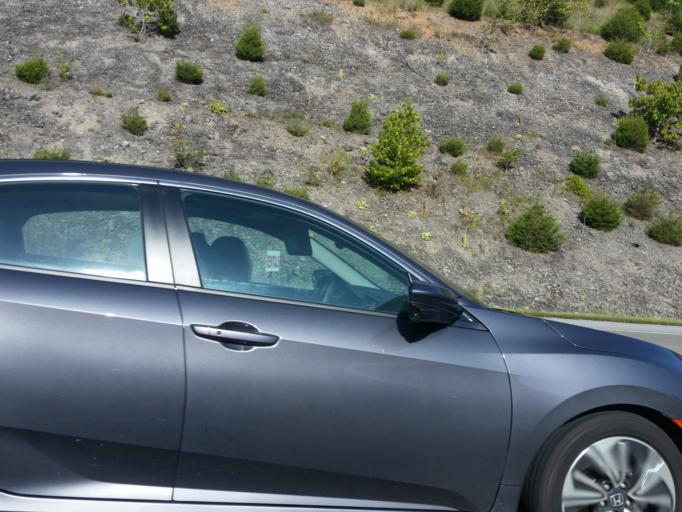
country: US
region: Tennessee
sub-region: Claiborne County
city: Harrogate
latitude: 36.5362
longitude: -83.6289
